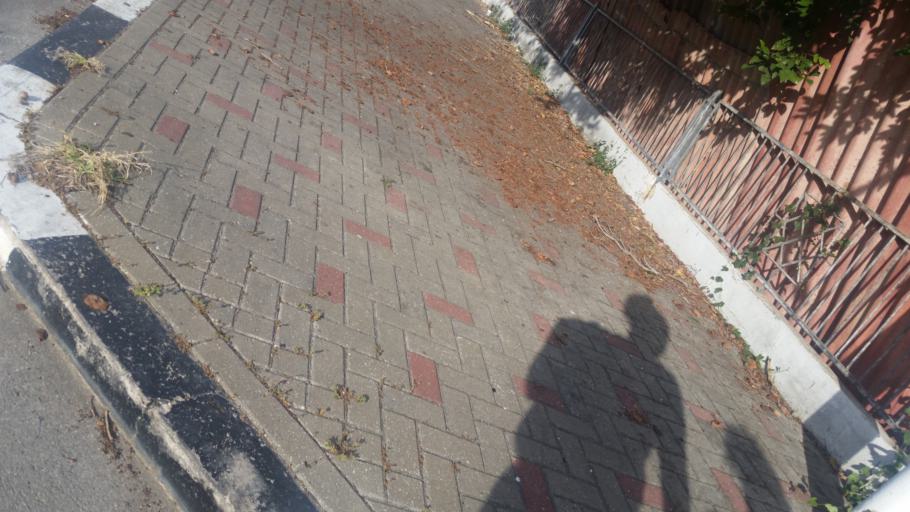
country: CW
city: Willemstad
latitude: 12.1472
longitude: -68.9241
